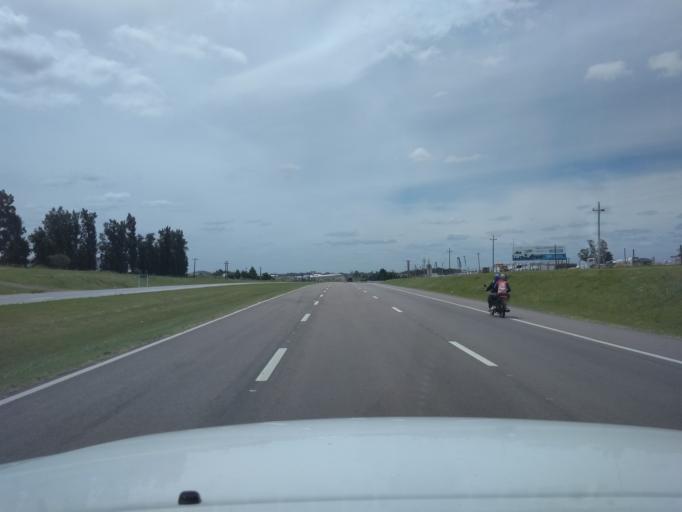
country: UY
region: Canelones
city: Las Piedras
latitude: -34.7040
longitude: -56.2406
